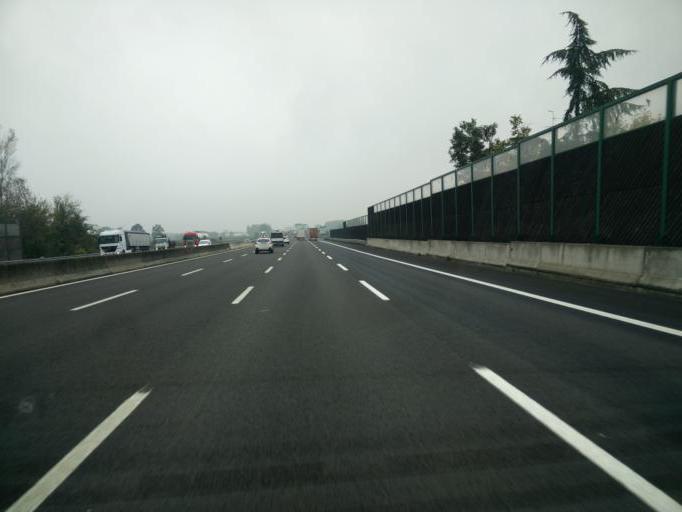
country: IT
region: Emilia-Romagna
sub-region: Provincia di Modena
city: Baggiovara
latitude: 44.6374
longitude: 10.8732
